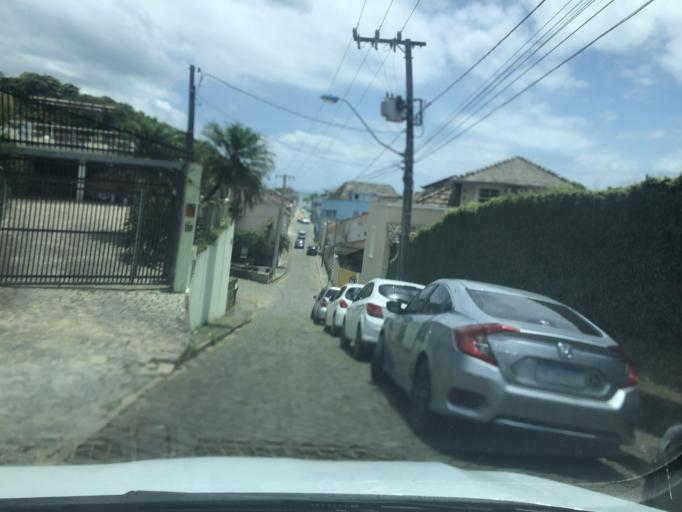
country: BR
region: Santa Catarina
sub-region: Sao Francisco Do Sul
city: Sao Francisco do Sul
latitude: -26.2450
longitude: -48.6389
